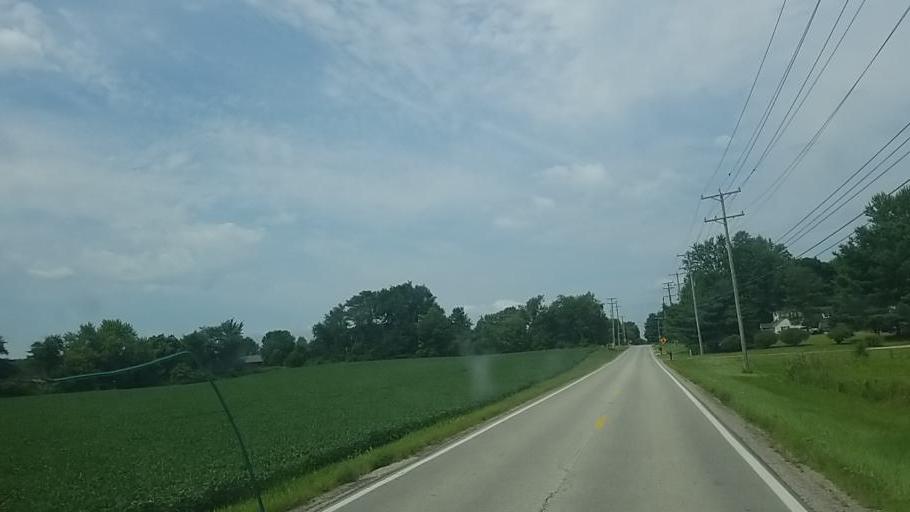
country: US
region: Ohio
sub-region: Franklin County
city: New Albany
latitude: 40.1140
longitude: -82.8350
